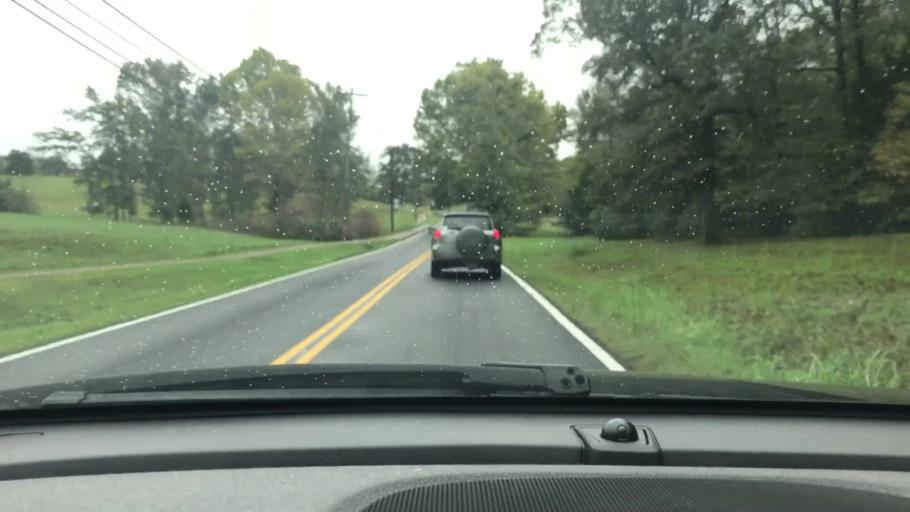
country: US
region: Tennessee
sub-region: Cheatham County
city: Kingston Springs
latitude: 36.0953
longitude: -87.1112
